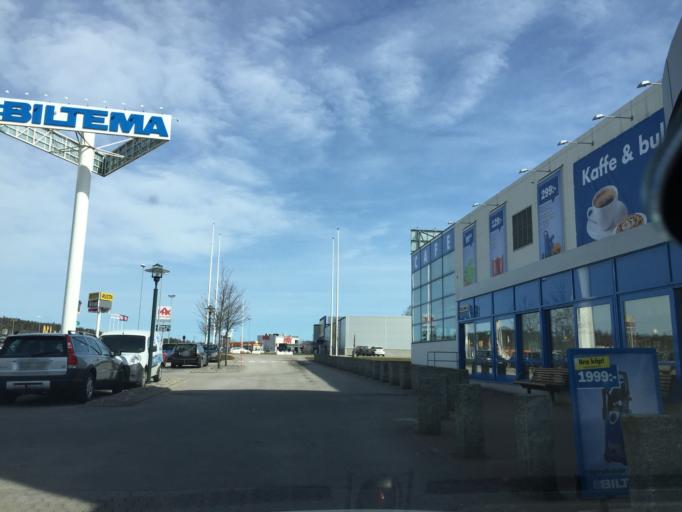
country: SE
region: Vaestra Goetaland
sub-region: Uddevalla Kommun
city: Uddevalla
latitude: 58.3506
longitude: 11.8073
